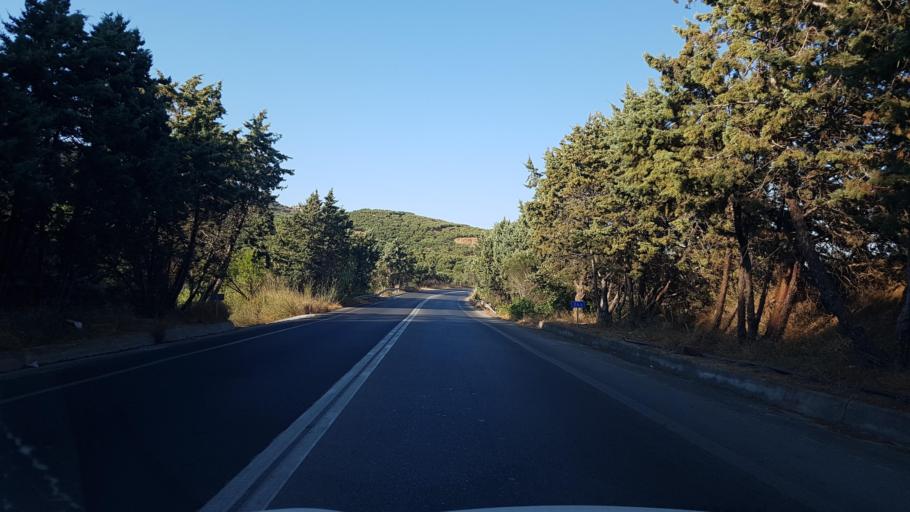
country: GR
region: Crete
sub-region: Nomos Chanias
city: Kolympari
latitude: 35.5338
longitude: 23.7707
